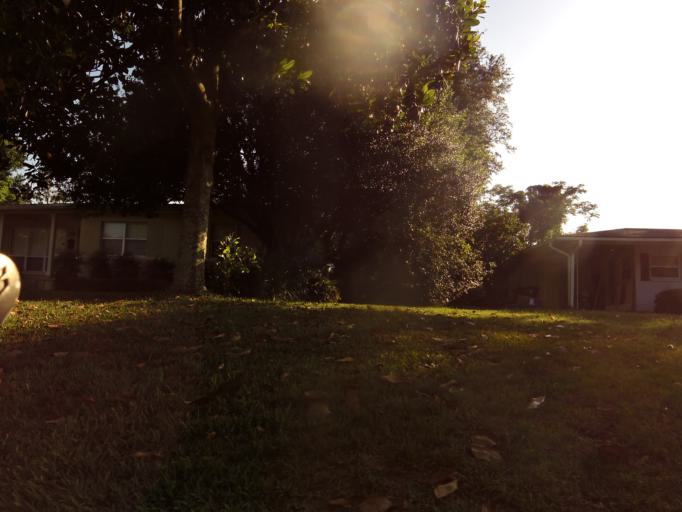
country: US
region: Florida
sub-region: Duval County
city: Jacksonville
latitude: 30.2409
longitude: -81.6146
